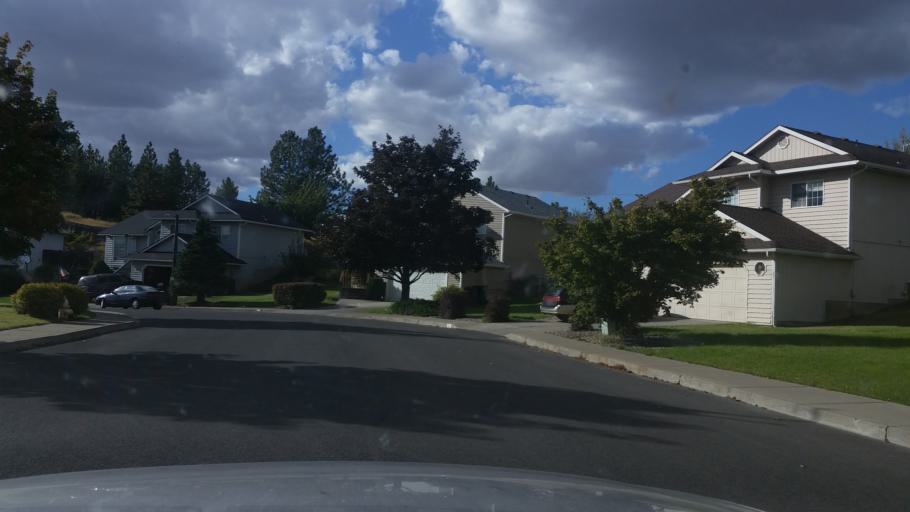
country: US
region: Washington
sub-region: Spokane County
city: Cheney
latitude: 47.4833
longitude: -117.6007
